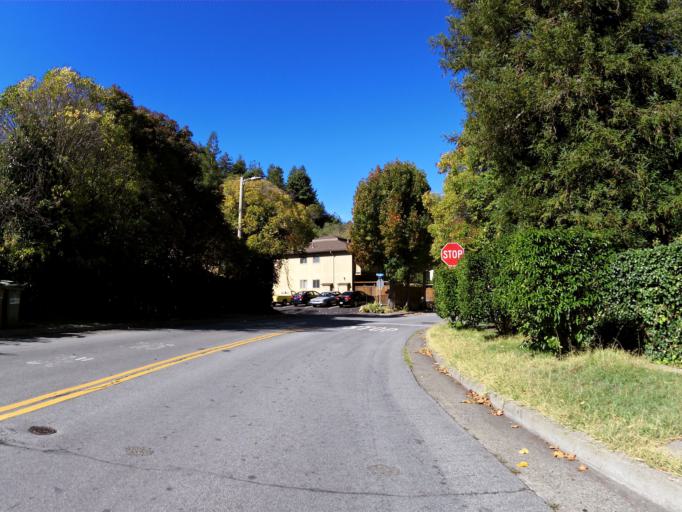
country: US
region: California
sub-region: Marin County
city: Kentfield
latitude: 37.9545
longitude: -122.5520
